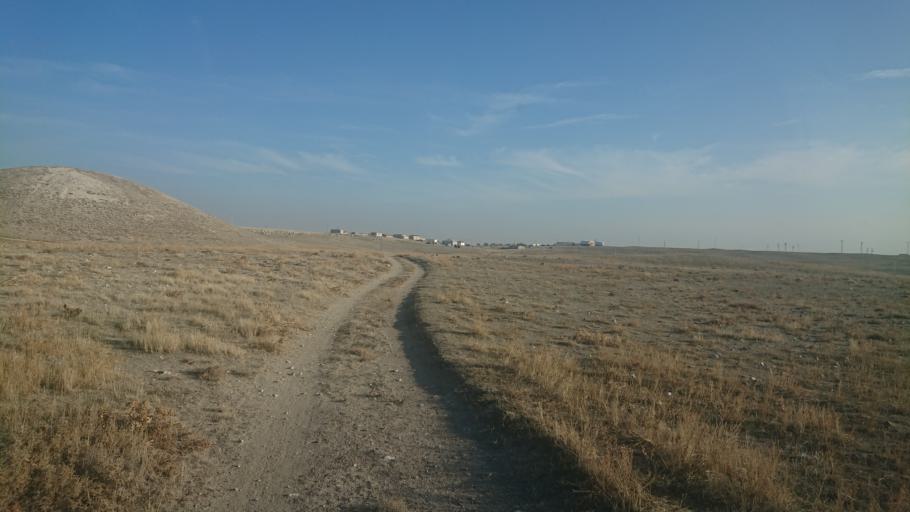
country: TR
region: Aksaray
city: Sultanhani
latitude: 38.1446
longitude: 33.5823
